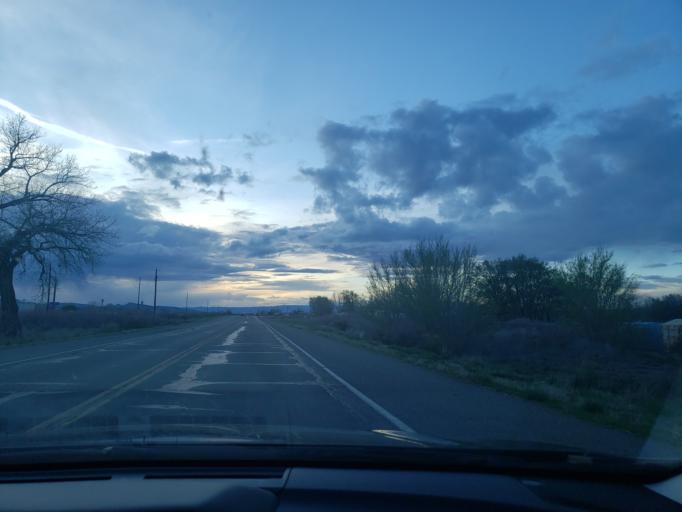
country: US
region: Colorado
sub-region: Mesa County
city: Fruita
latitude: 39.1410
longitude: -108.7050
